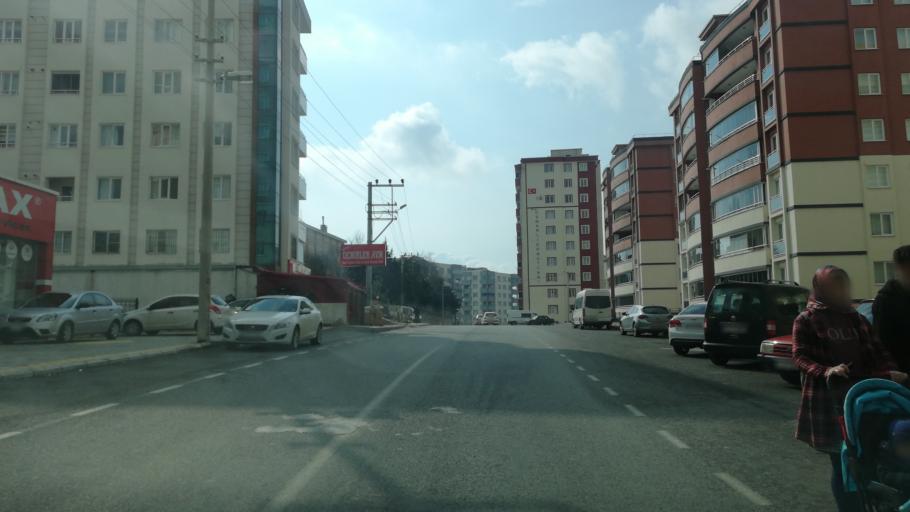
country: TR
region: Kahramanmaras
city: Kahramanmaras
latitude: 37.5799
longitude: 36.8962
